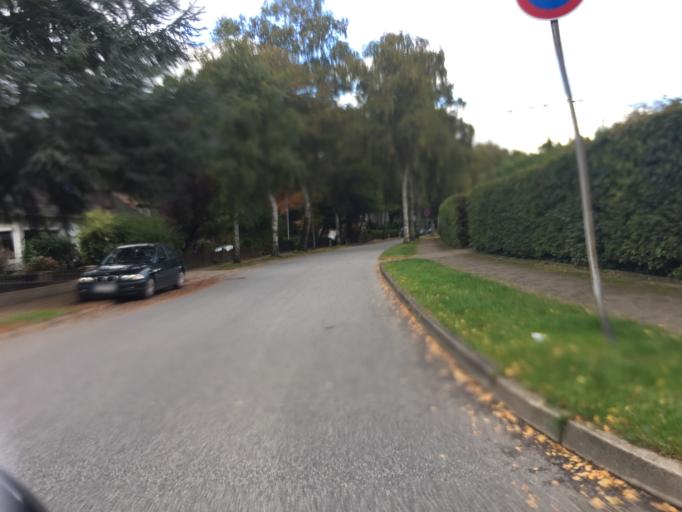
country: DE
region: Schleswig-Holstein
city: Itzehoe
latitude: 53.9432
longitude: 9.5099
